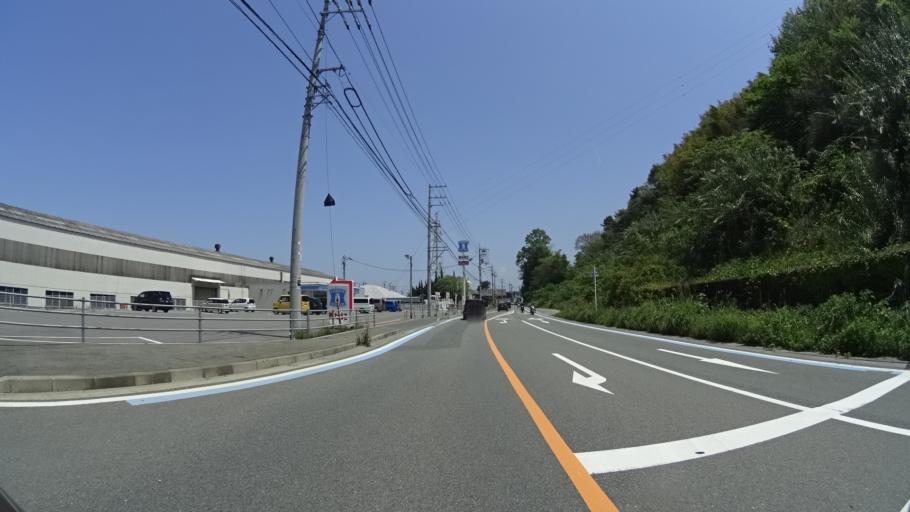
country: JP
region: Ehime
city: Ozu
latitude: 33.6213
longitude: 132.4993
